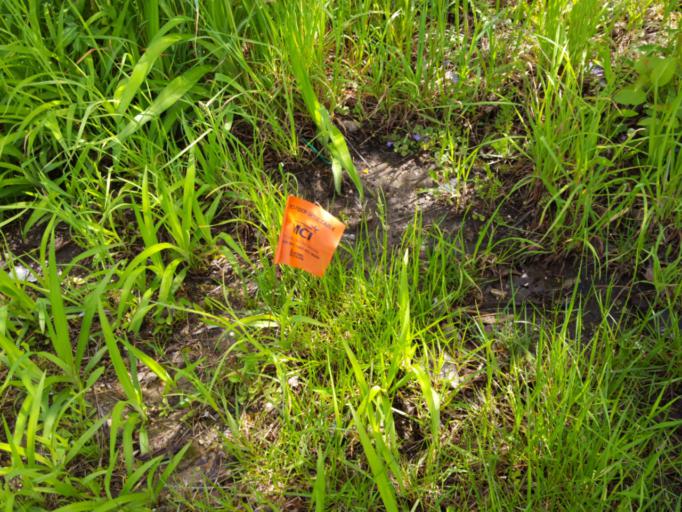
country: US
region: Illinois
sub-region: Cook County
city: Northbrook
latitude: 42.1463
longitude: -87.8310
